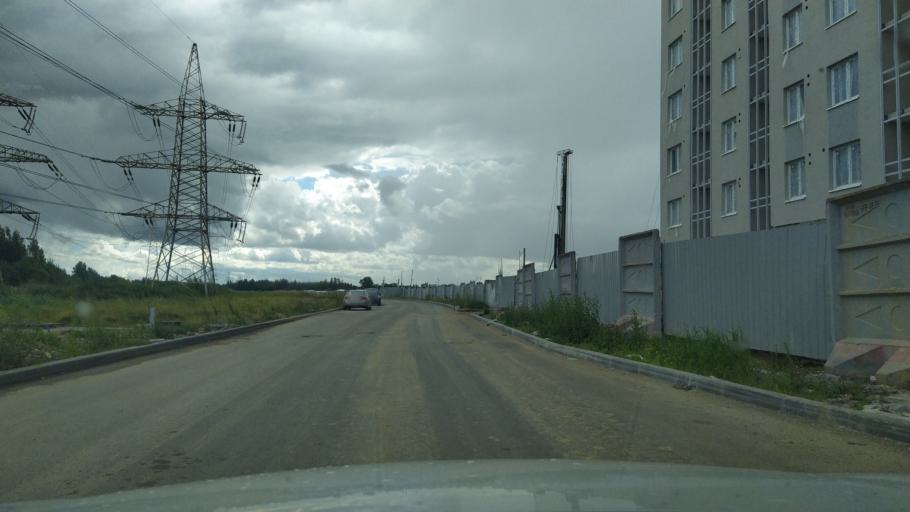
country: RU
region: St.-Petersburg
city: Krasnogvargeisky
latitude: 60.0030
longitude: 30.4831
